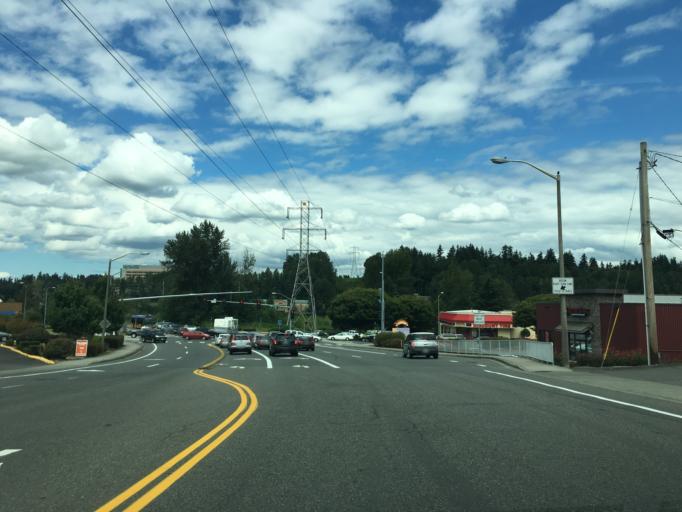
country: US
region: Washington
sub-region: King County
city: Kingsgate
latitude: 47.7080
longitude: -122.1757
